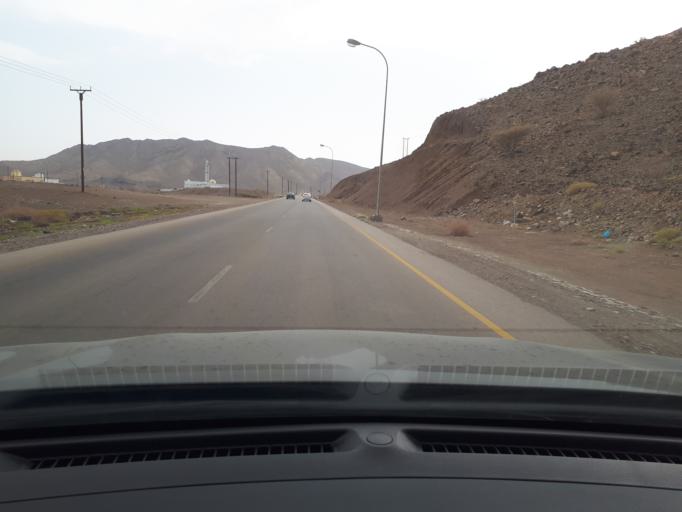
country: OM
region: Ash Sharqiyah
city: Badiyah
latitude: 22.5438
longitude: 58.9905
